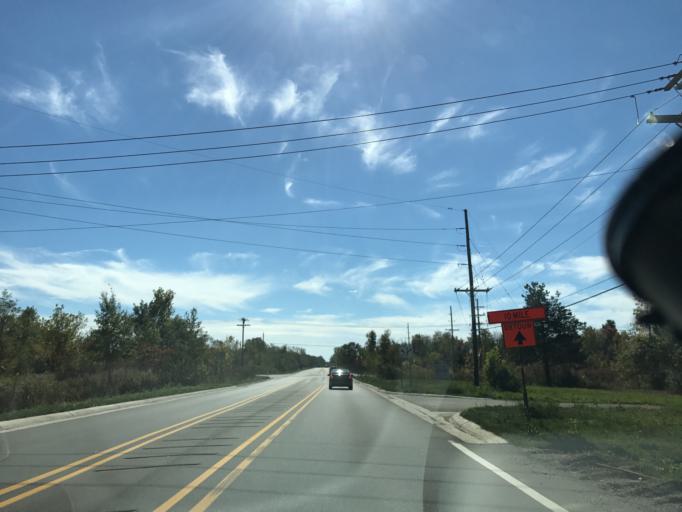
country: US
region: Michigan
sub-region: Oakland County
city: South Lyon
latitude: 42.4482
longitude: -83.6310
